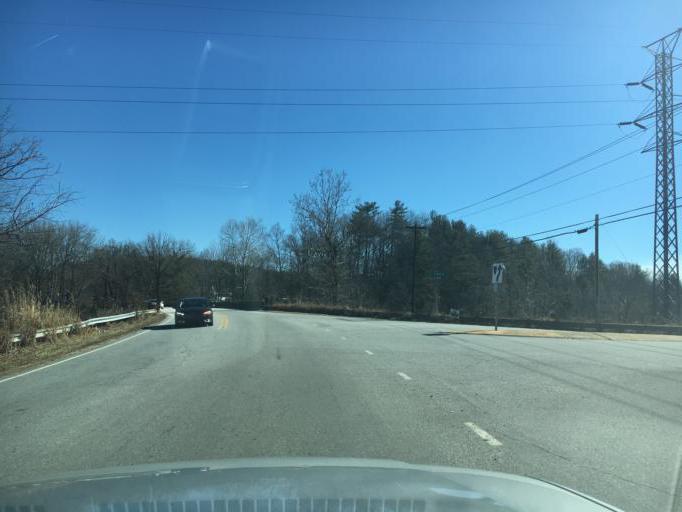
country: US
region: North Carolina
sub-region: Henderson County
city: Fletcher
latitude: 35.4060
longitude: -82.5166
